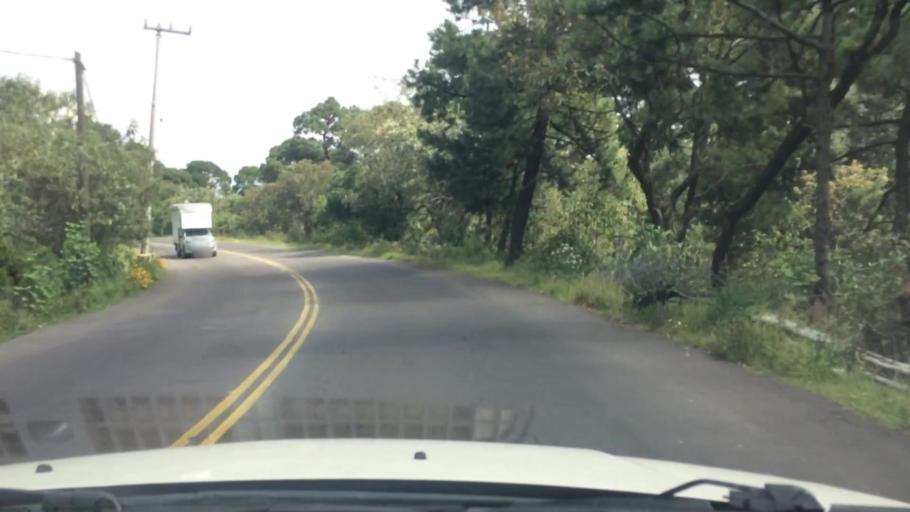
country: MX
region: Mexico City
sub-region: Tlalpan
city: Lomas de Tepemecatl
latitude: 19.2594
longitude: -99.2373
